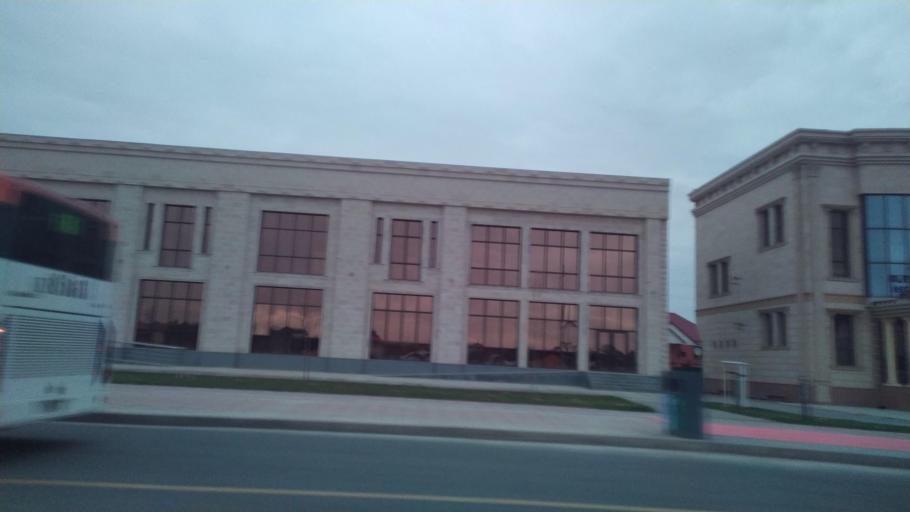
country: KZ
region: Ongtustik Qazaqstan
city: Turkestan
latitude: 43.2802
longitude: 68.3216
